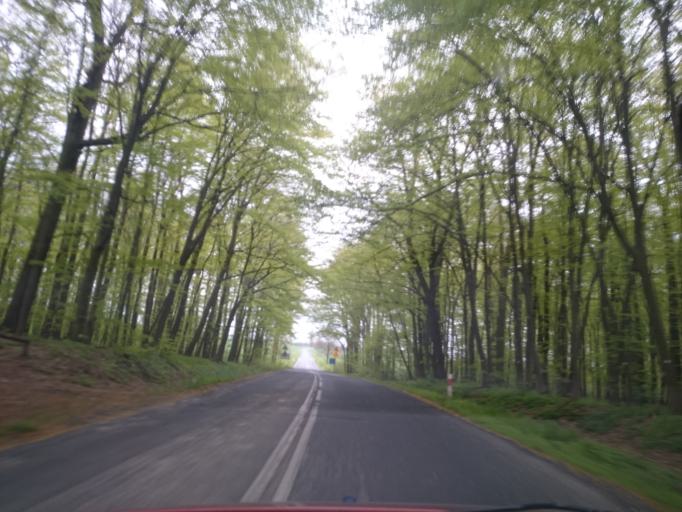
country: PL
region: Lower Silesian Voivodeship
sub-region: Powiat strzelinski
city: Przeworno
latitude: 50.6550
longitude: 17.2348
